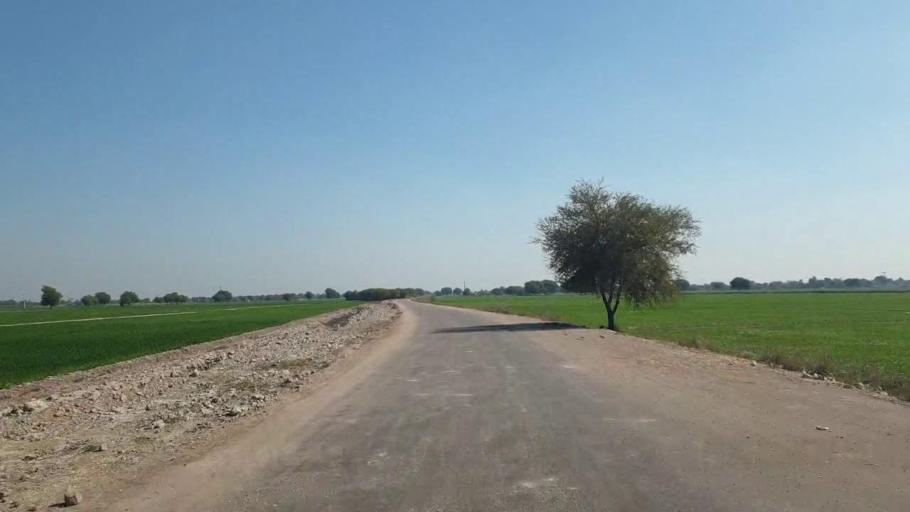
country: PK
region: Sindh
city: Shahpur Chakar
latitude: 26.1301
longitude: 68.6327
